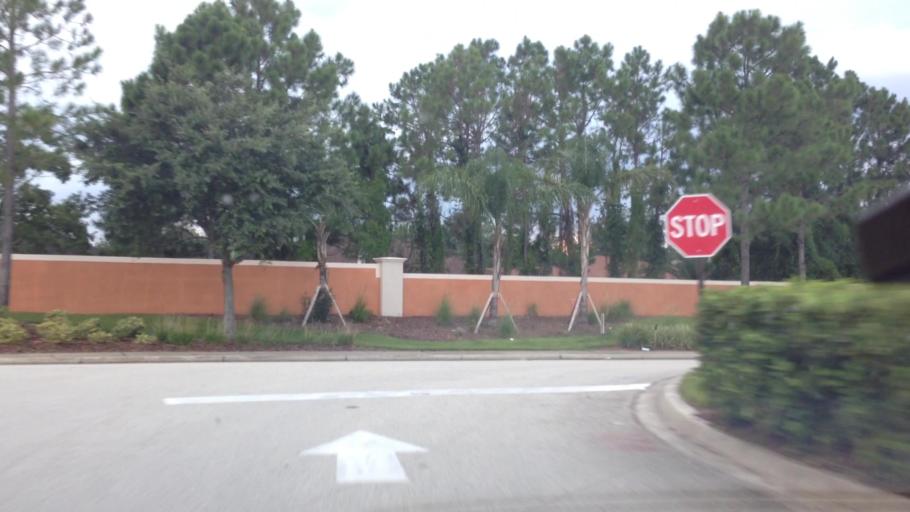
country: US
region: Florida
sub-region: Duval County
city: Atlantic Beach
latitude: 30.3200
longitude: -81.4958
